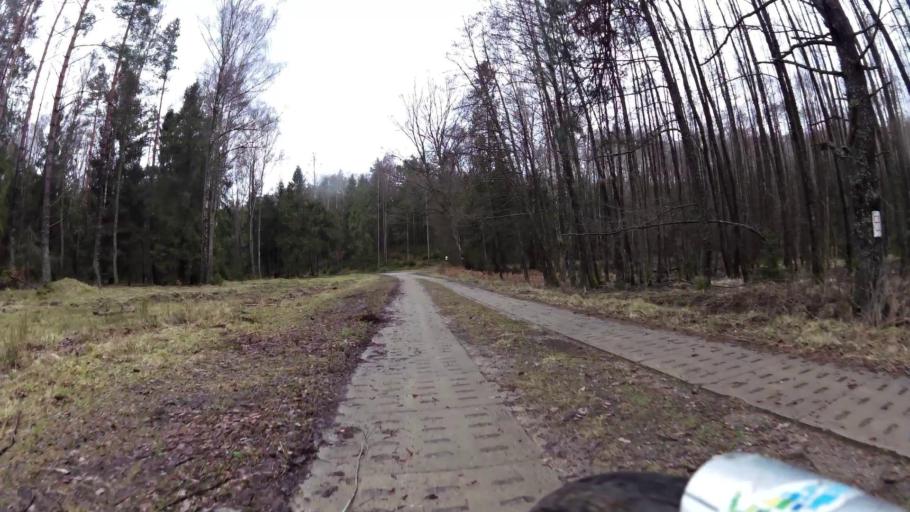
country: PL
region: Pomeranian Voivodeship
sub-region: Powiat bytowski
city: Kolczyglowy
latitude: 54.2442
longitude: 17.2779
